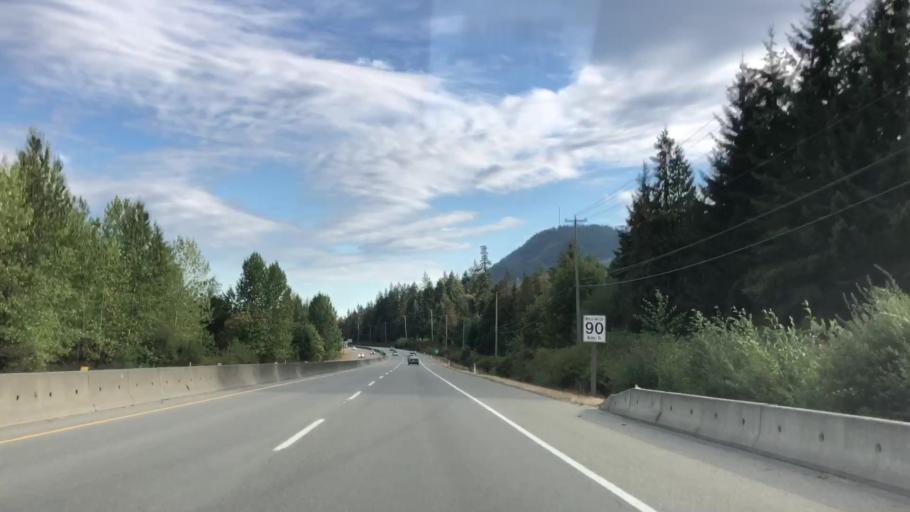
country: CA
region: British Columbia
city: North Saanich
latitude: 48.6247
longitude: -123.5472
